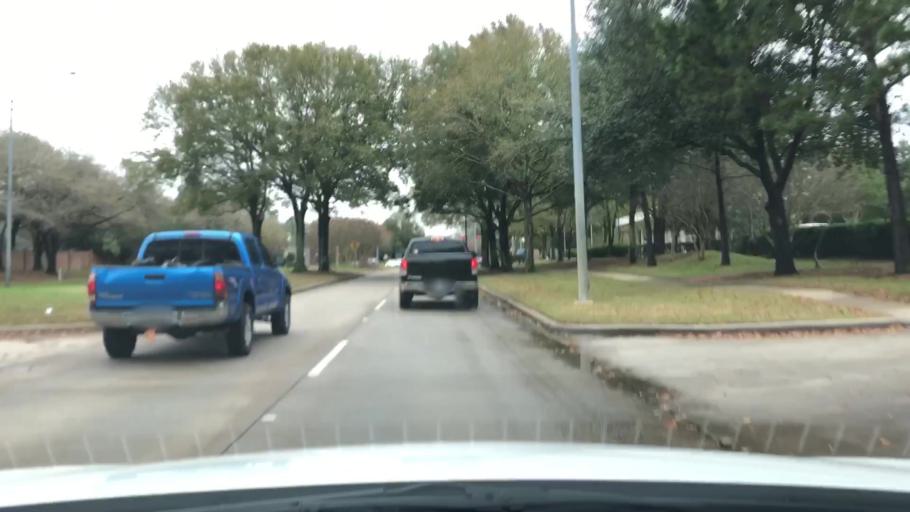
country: US
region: Texas
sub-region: Fort Bend County
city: Cinco Ranch
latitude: 29.7420
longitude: -95.7513
